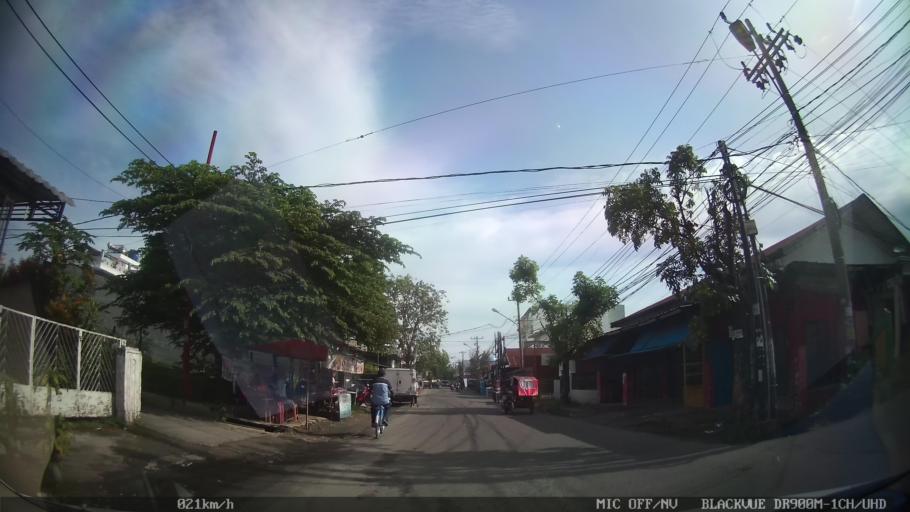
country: ID
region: North Sumatra
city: Medan
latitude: 3.6117
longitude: 98.6452
